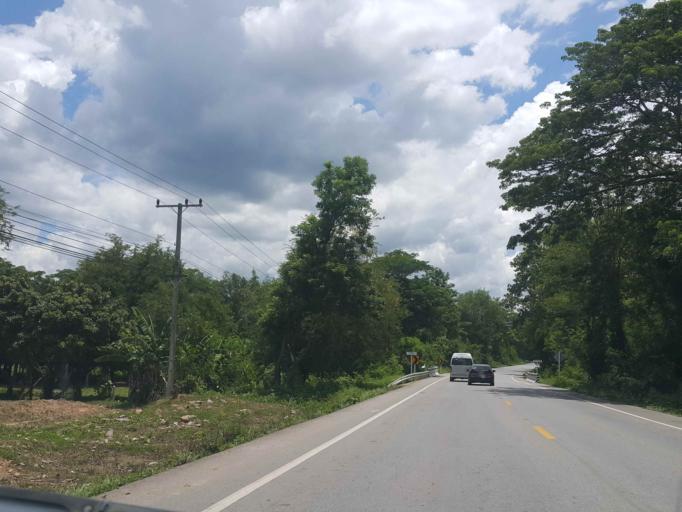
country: TH
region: Nan
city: Wiang Sa
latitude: 18.5202
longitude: 100.5845
